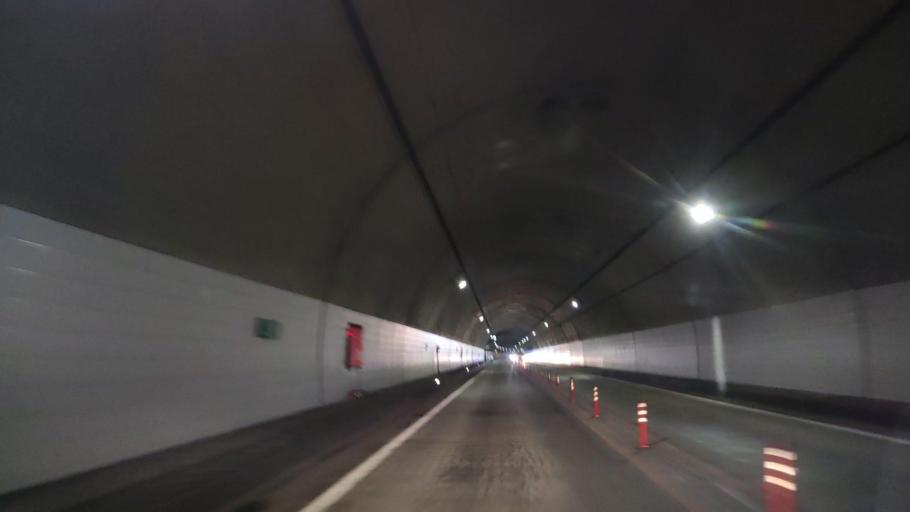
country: JP
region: Akita
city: Odate
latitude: 40.3642
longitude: 140.6968
